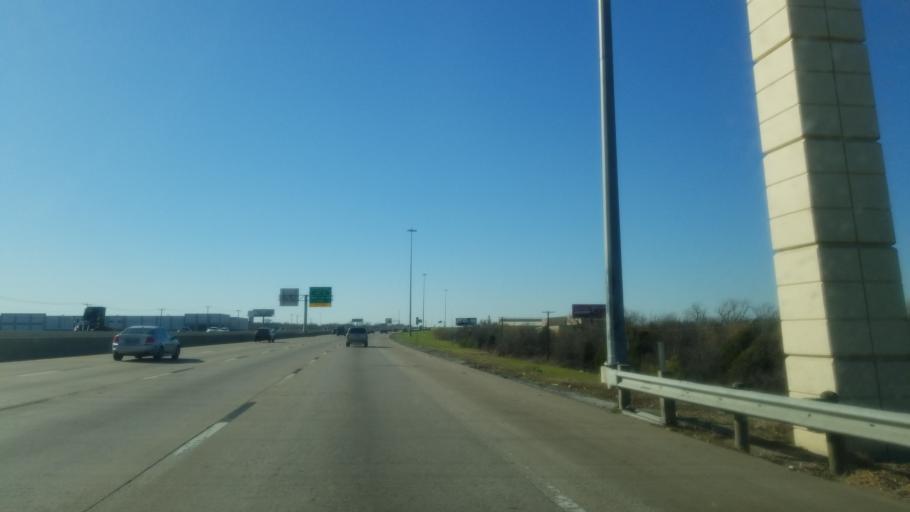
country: US
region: Texas
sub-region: Dallas County
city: Irving
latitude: 32.7631
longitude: -96.9457
